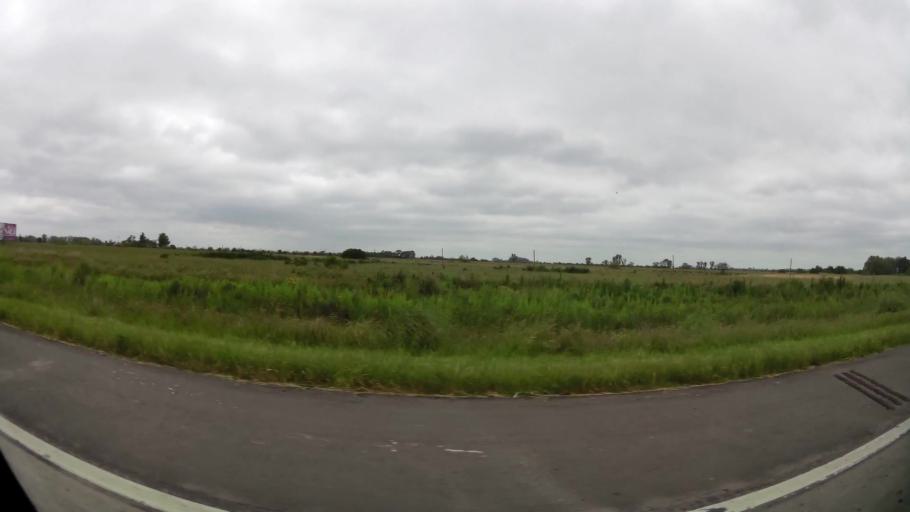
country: AR
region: Buenos Aires
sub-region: Partido de San Vicente
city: San Vicente
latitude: -35.0293
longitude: -58.3668
